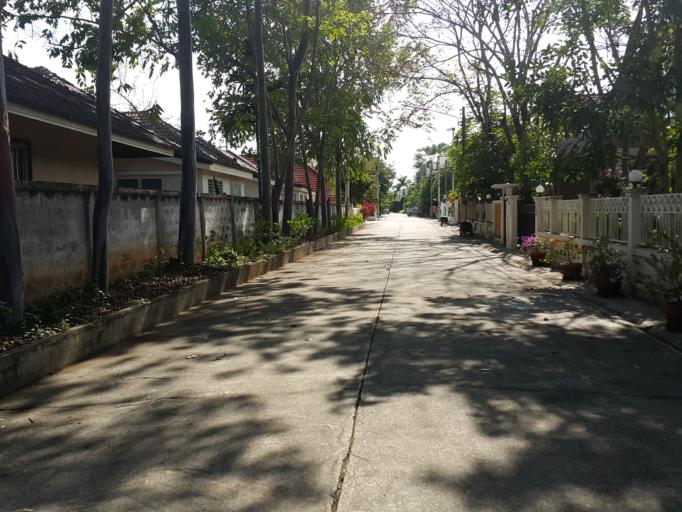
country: TH
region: Chiang Mai
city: San Sai
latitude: 18.8646
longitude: 99.1113
